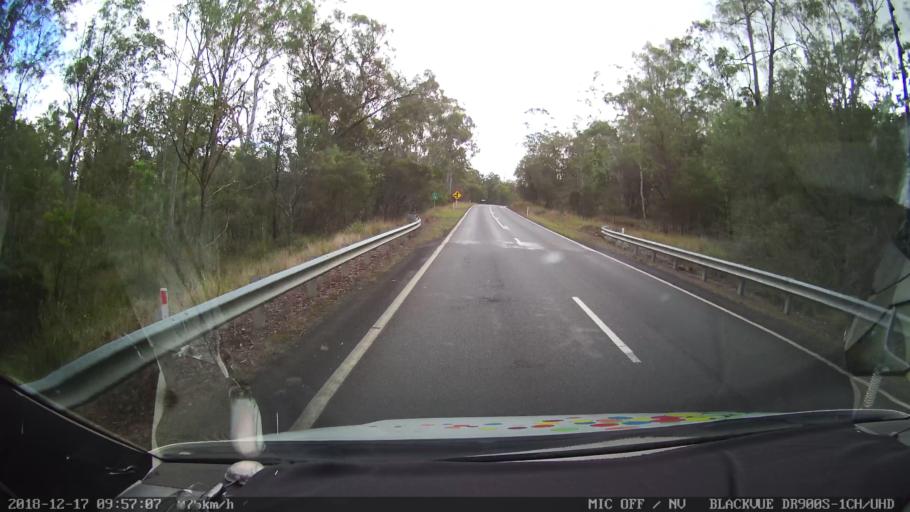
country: AU
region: New South Wales
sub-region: Tenterfield Municipality
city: Carrolls Creek
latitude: -28.9278
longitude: 152.3944
